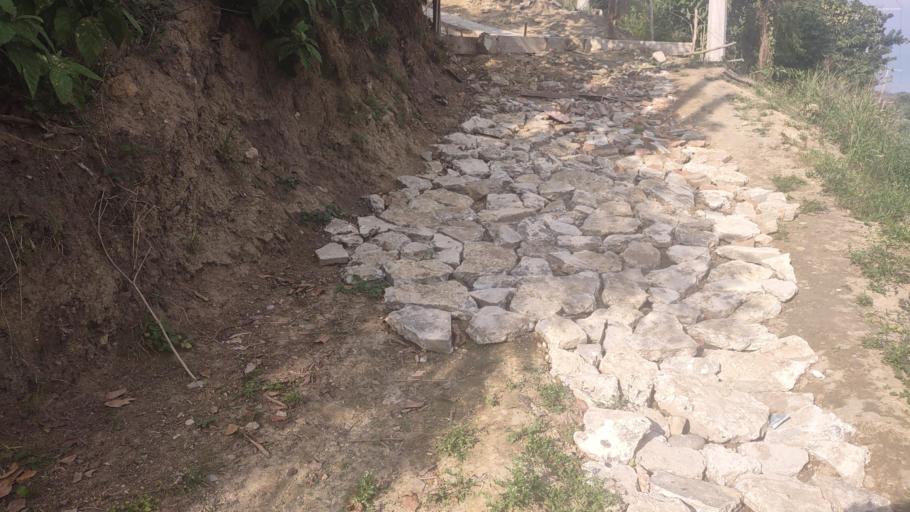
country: MX
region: Veracruz
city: Papantla de Olarte
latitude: 20.4476
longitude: -97.3084
